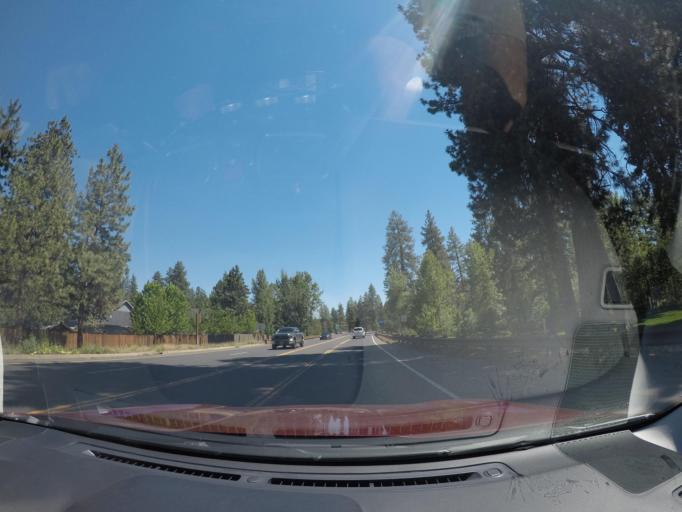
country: US
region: Oregon
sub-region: Deschutes County
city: Sisters
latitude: 44.2890
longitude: -121.5420
